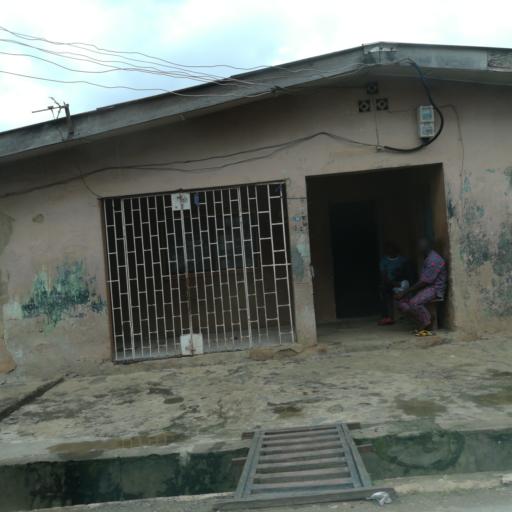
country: NG
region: Lagos
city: Agege
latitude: 6.6041
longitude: 3.2976
